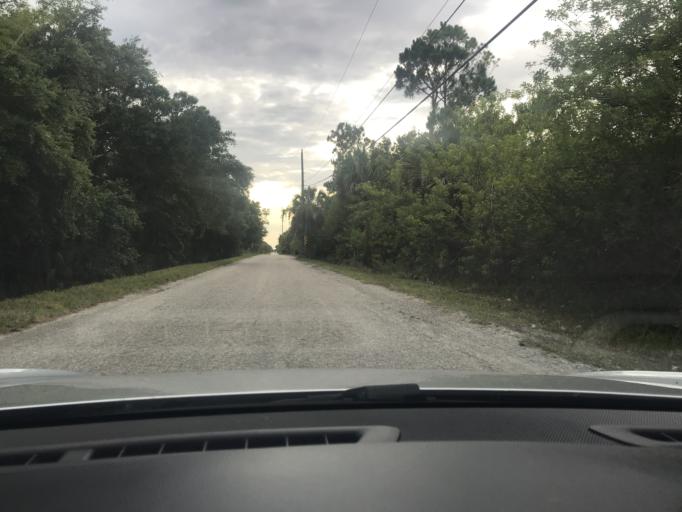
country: US
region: Florida
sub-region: Indian River County
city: Gifford
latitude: 27.6827
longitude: -80.4521
